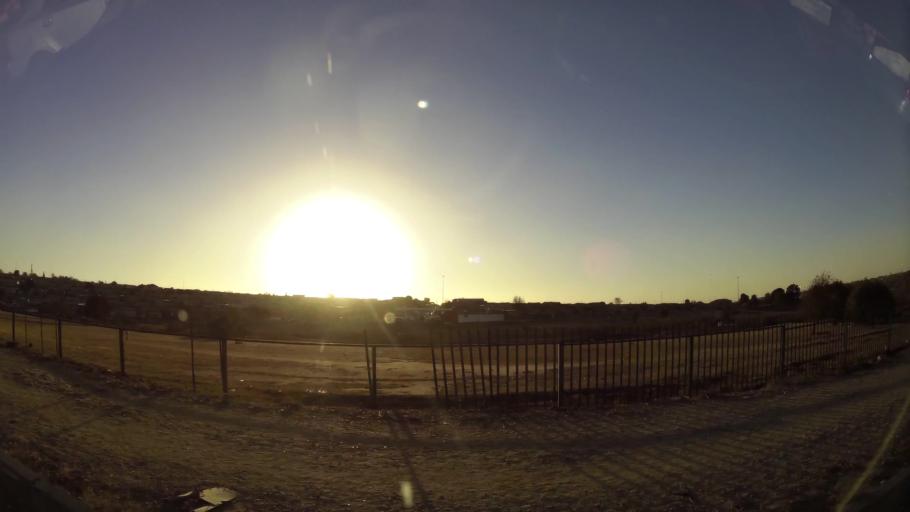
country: ZA
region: Gauteng
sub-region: Ekurhuleni Metropolitan Municipality
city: Tembisa
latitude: -26.0188
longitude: 28.2010
